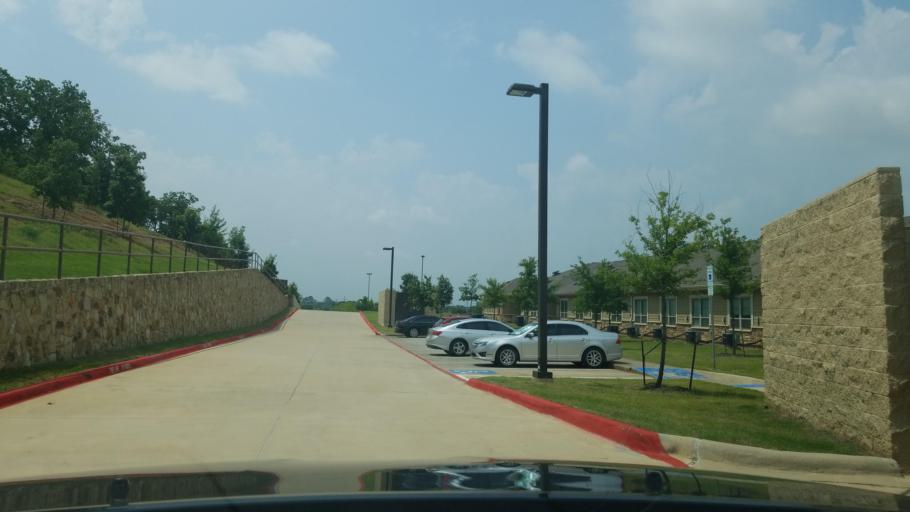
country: US
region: Texas
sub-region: Denton County
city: Corinth
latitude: 33.1881
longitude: -97.0942
